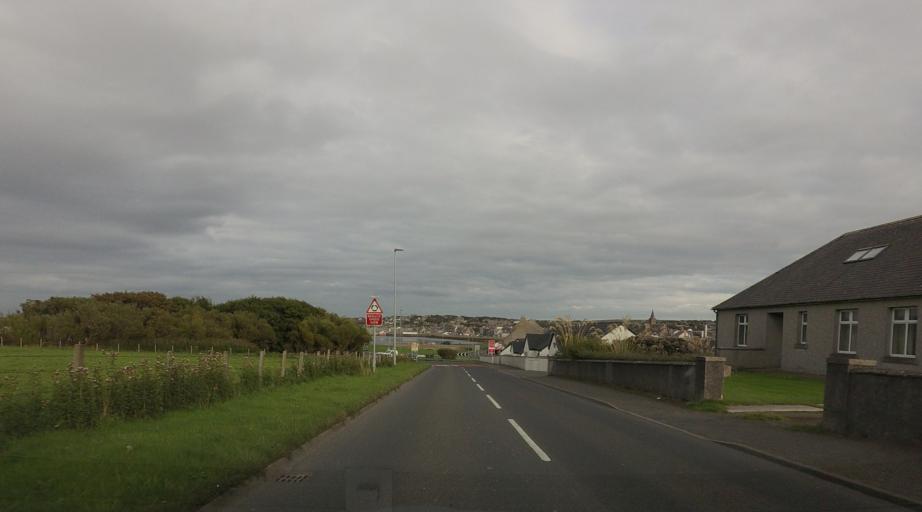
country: GB
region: Scotland
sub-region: Orkney Islands
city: Orkney
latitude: 58.9864
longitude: -2.9733
